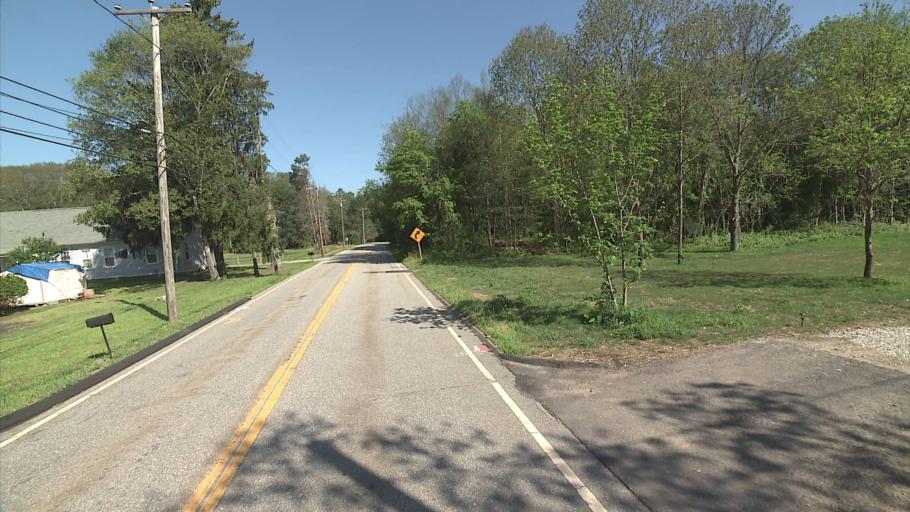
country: US
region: Connecticut
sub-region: New London County
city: Montville Center
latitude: 41.4674
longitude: -72.1598
